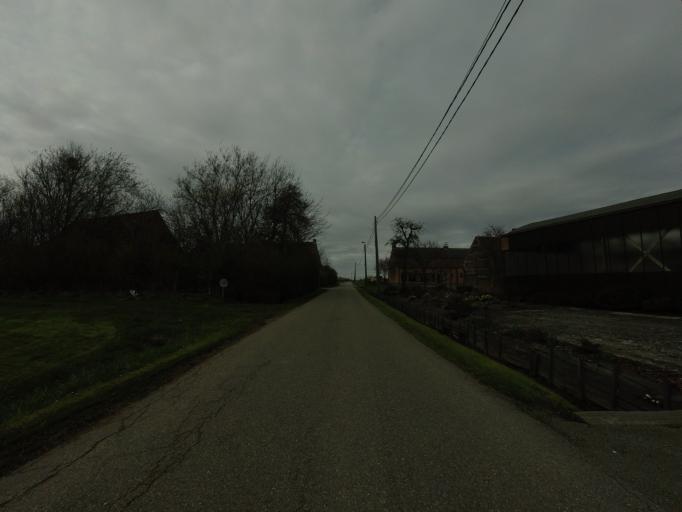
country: BE
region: Flanders
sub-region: Provincie Antwerpen
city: Lint
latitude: 51.1380
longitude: 4.5270
